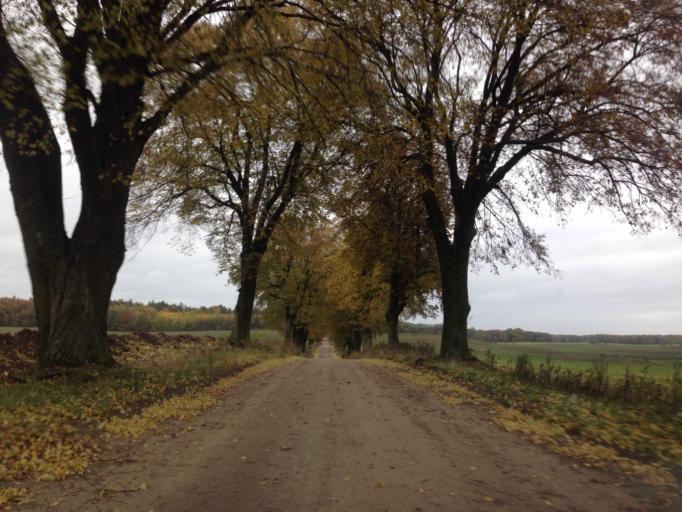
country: PL
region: Warmian-Masurian Voivodeship
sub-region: Powiat ilawski
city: Susz
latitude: 53.6744
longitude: 19.2909
